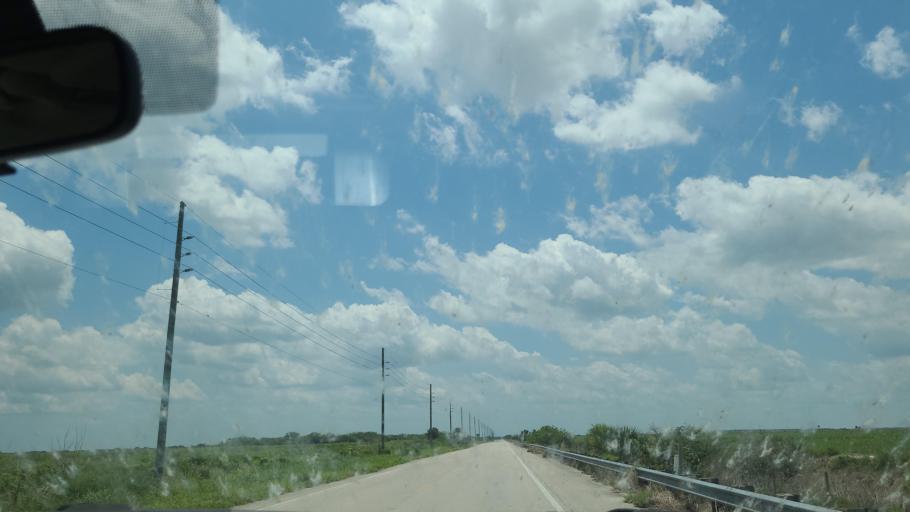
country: US
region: Florida
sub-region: Glades County
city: Buckhead Ridge
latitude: 27.1853
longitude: -81.0940
